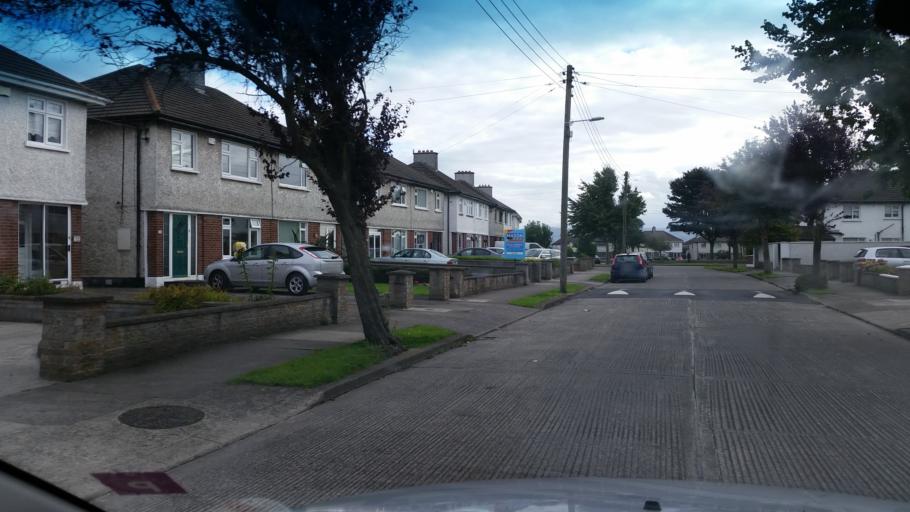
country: IE
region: Leinster
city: Ballymun
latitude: 53.3884
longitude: -6.2755
